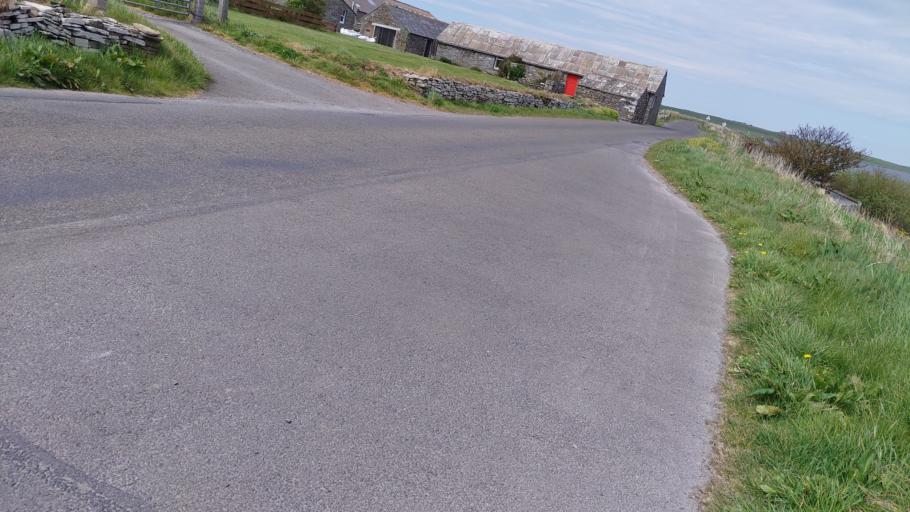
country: GB
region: Scotland
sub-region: Orkney Islands
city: Stromness
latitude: 58.9978
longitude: -3.2156
